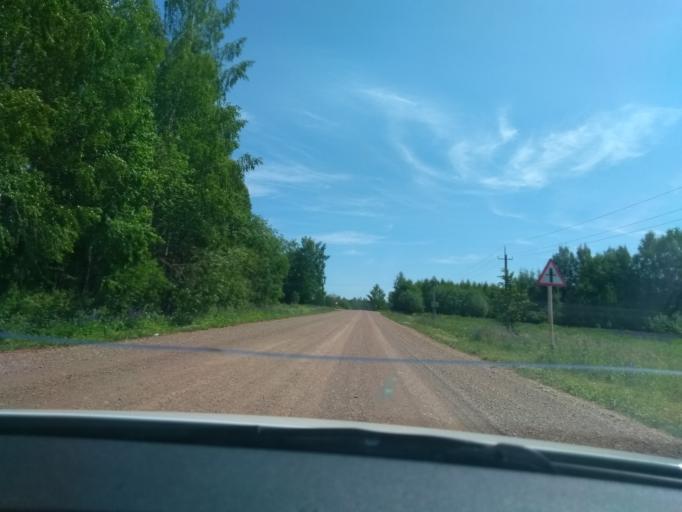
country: RU
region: Perm
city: Sylva
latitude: 57.8170
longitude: 56.7264
